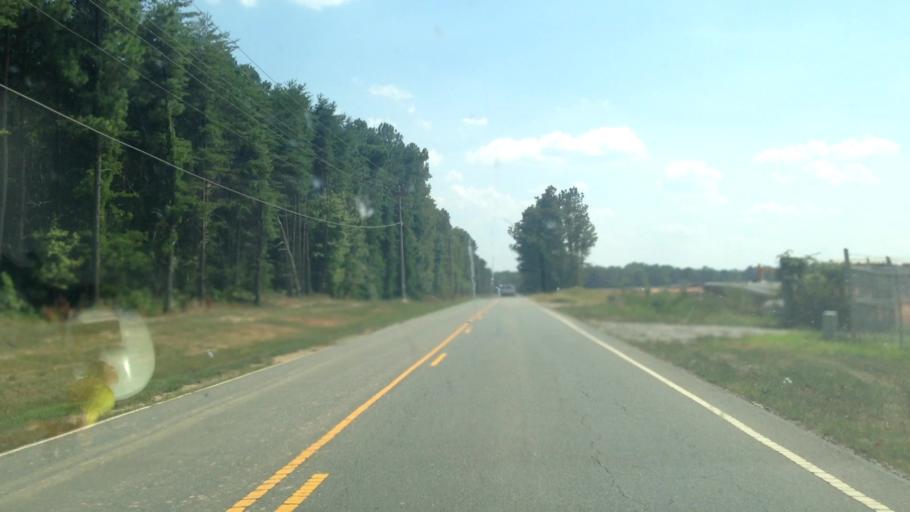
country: US
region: North Carolina
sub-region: Stokes County
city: Walnut Cove
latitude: 36.2952
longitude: -80.0625
